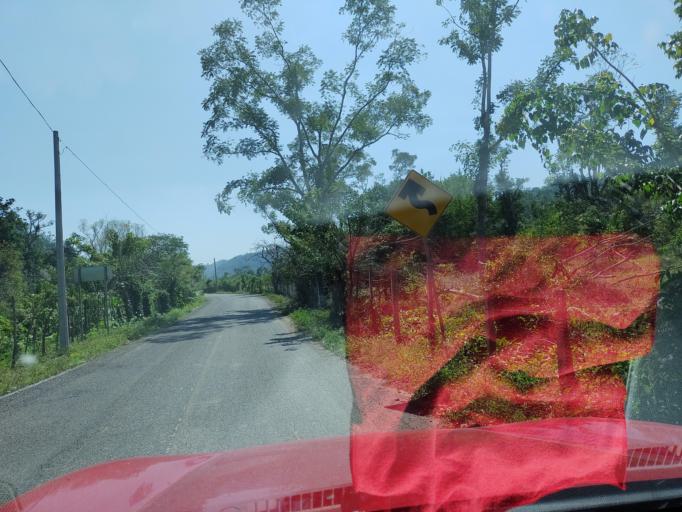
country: MX
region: Veracruz
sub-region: Papantla
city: Polutla
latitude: 20.4995
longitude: -97.2136
